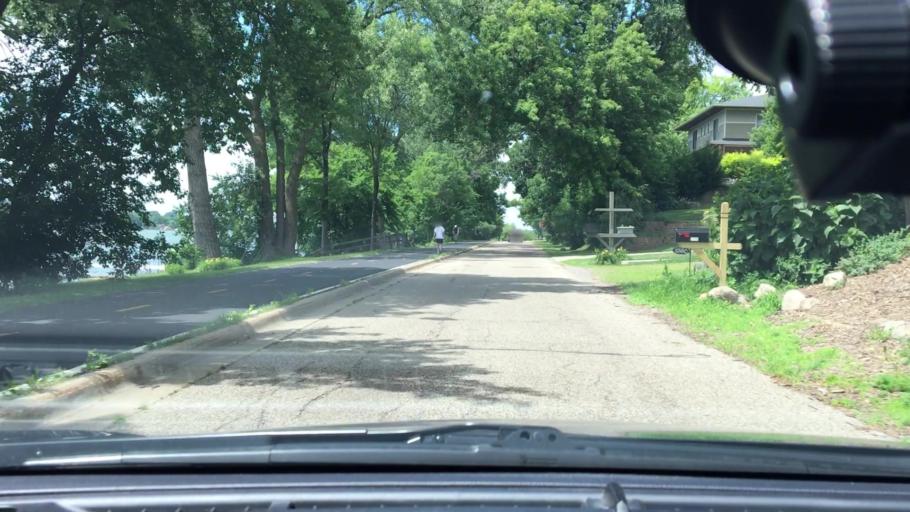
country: US
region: Minnesota
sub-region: Hennepin County
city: New Hope
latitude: 45.0066
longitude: -93.4085
